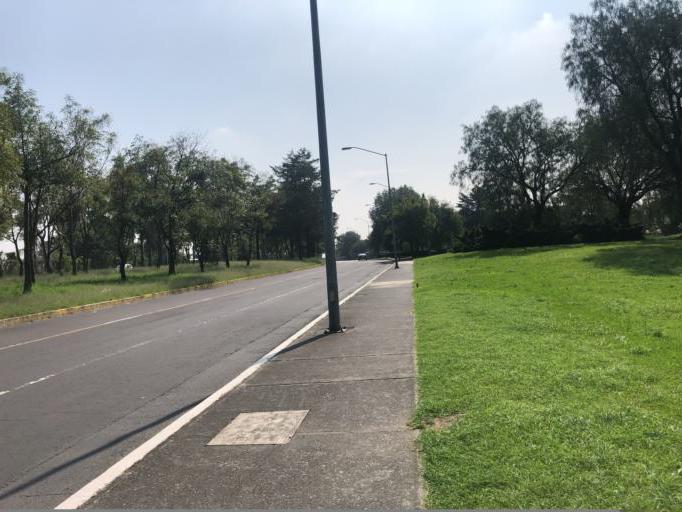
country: MX
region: Mexico City
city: Tlalpan
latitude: 19.3170
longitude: -99.1821
